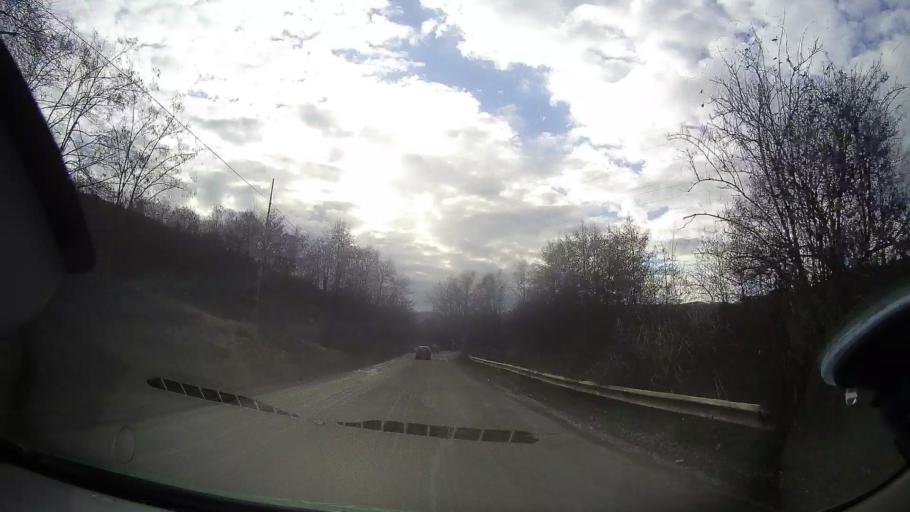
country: RO
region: Cluj
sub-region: Comuna Baisoara
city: Baisoara
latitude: 46.5829
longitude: 23.4627
